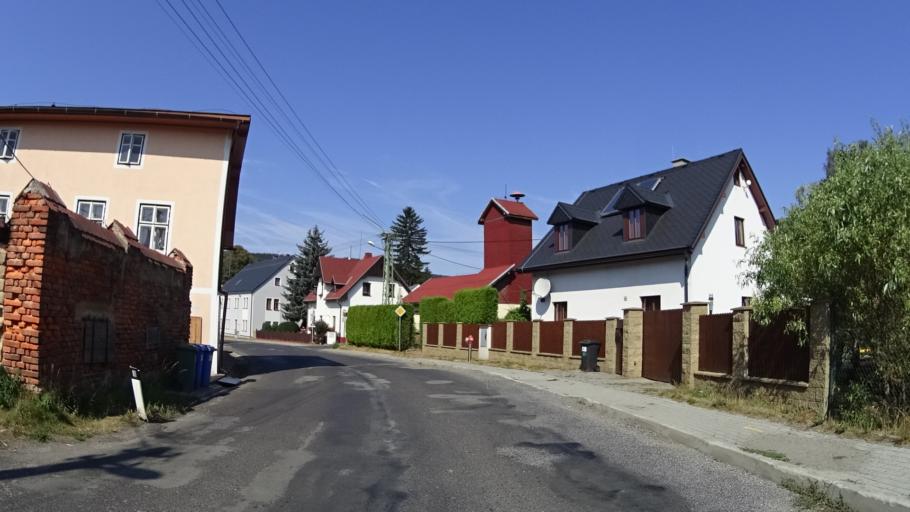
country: CZ
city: Straz nad Nisou
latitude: 50.7915
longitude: 14.9948
